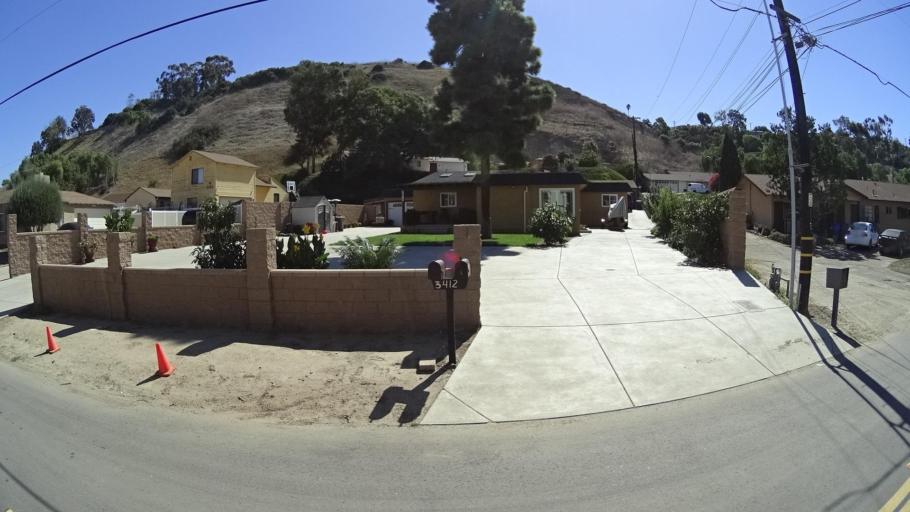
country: US
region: California
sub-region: San Diego County
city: Bonita
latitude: 32.6496
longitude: -117.0509
